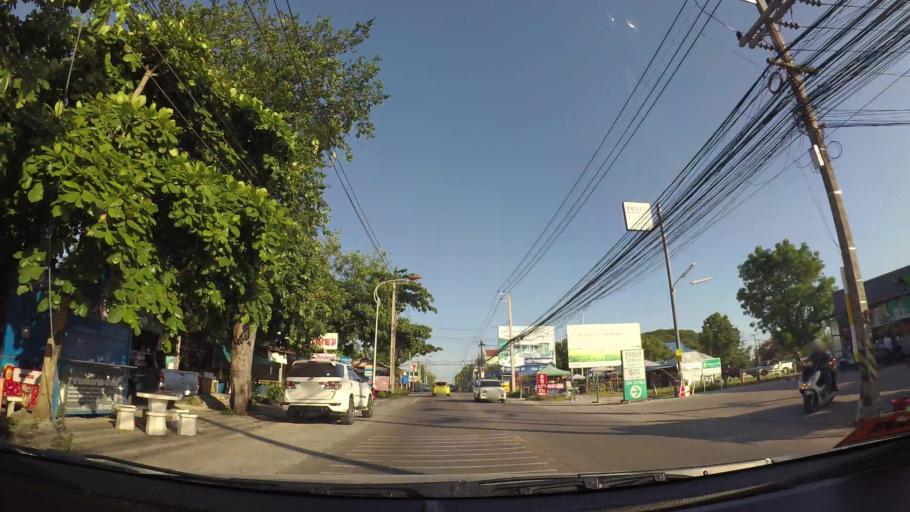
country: TH
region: Chon Buri
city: Si Racha
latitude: 13.1412
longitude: 100.9378
